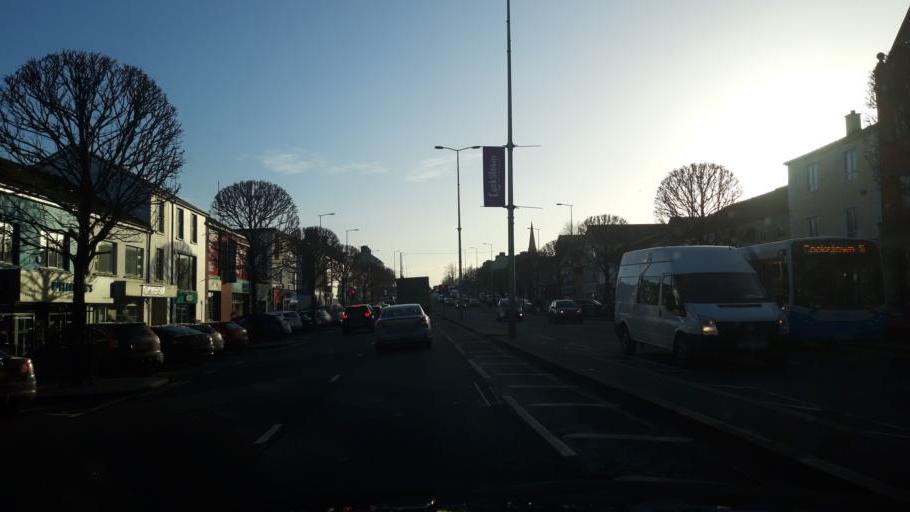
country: GB
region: Northern Ireland
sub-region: Cookstown District
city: Cookstown
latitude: 54.6468
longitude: -6.7451
